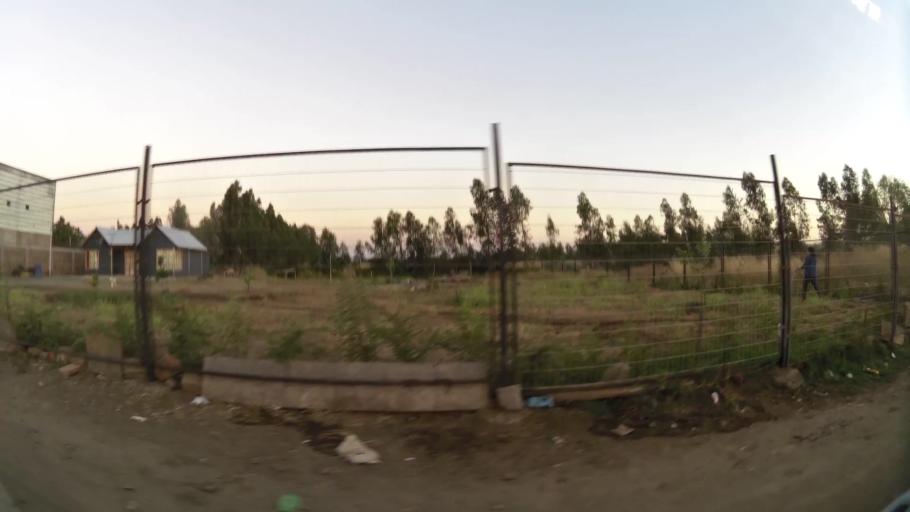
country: CL
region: Maule
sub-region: Provincia de Talca
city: Talca
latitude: -35.4503
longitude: -71.6260
